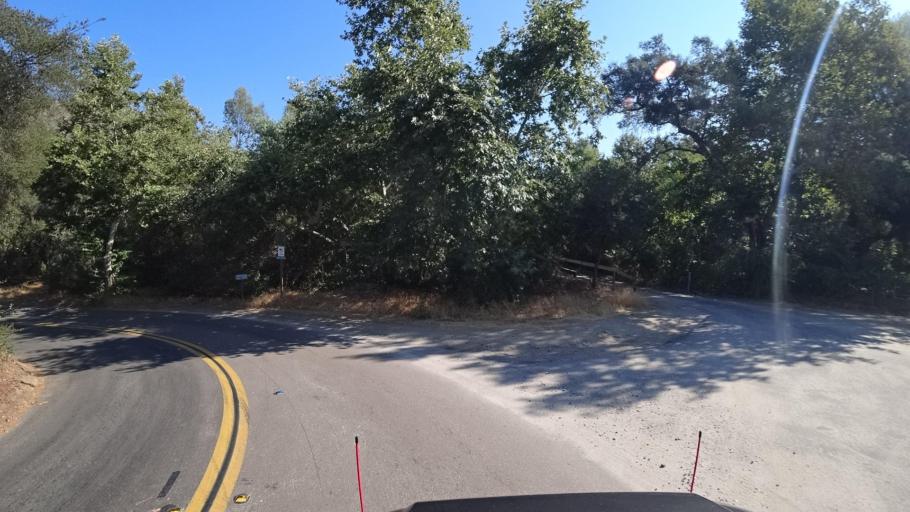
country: US
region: California
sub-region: San Diego County
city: Rainbow
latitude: 33.4072
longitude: -117.2005
